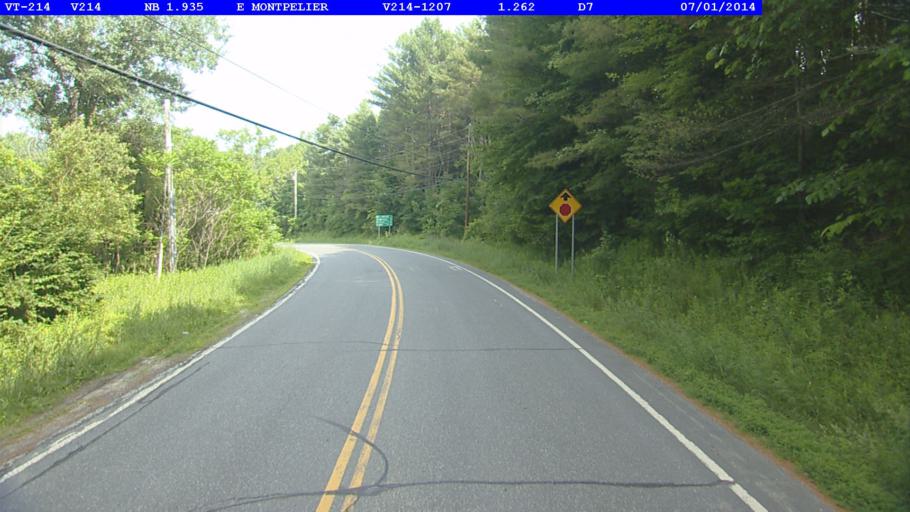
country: US
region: Vermont
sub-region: Washington County
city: Barre
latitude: 44.3029
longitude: -72.4446
